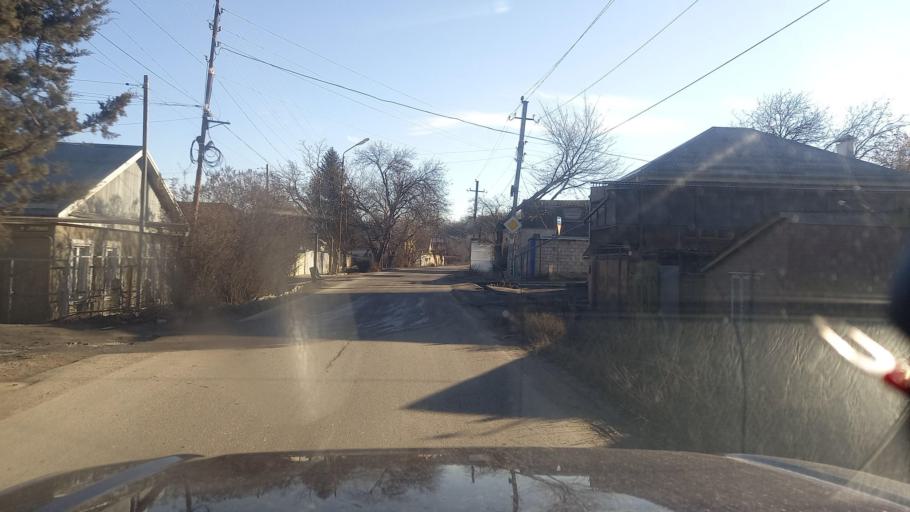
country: RU
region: Stavropol'skiy
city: Svobody
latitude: 44.0235
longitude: 43.0651
